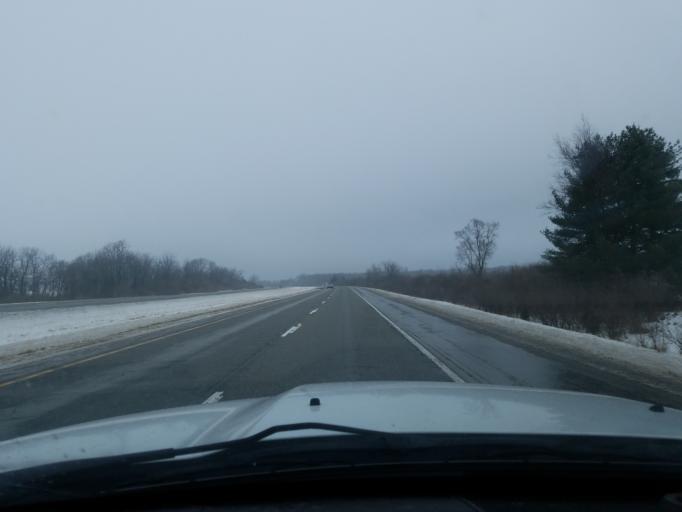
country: US
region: Indiana
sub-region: Fulton County
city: Rochester
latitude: 41.0050
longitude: -86.1675
